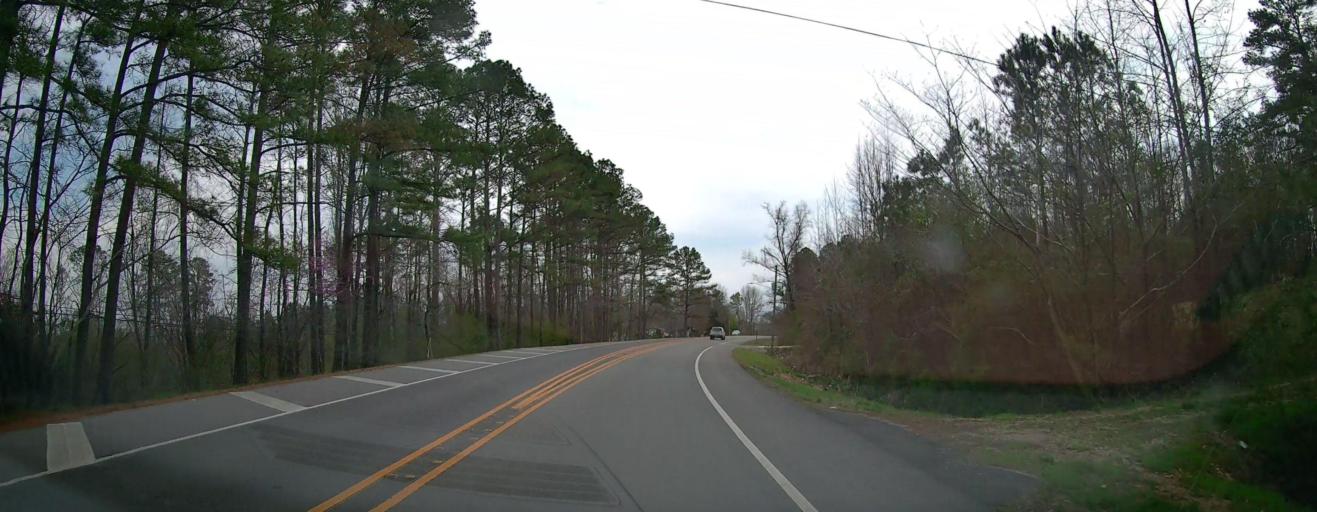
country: US
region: Alabama
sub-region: Marion County
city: Guin
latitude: 33.9833
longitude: -87.9181
